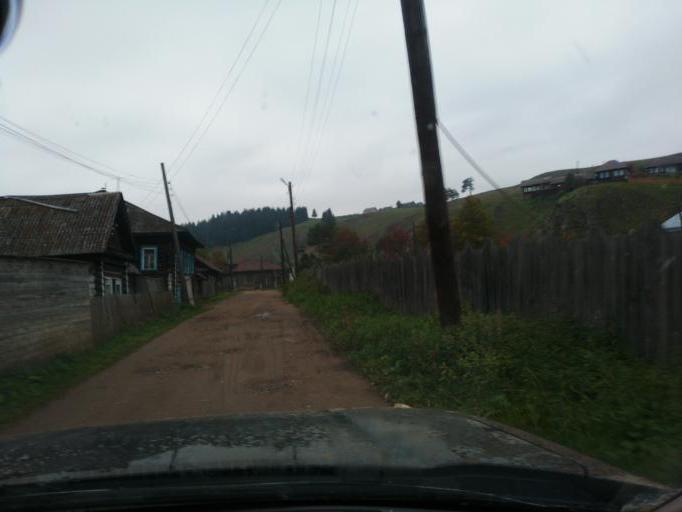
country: RU
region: Sverdlovsk
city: Sylva
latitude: 57.8673
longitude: 58.6498
